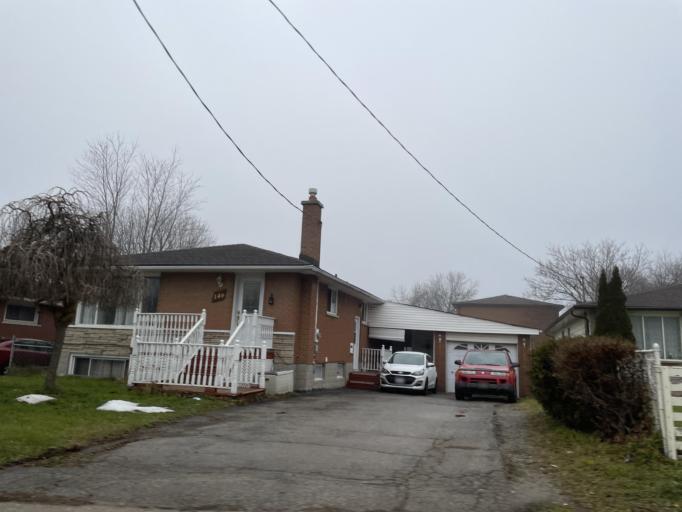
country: CA
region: Ontario
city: Kitchener
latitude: 43.4320
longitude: -80.4303
